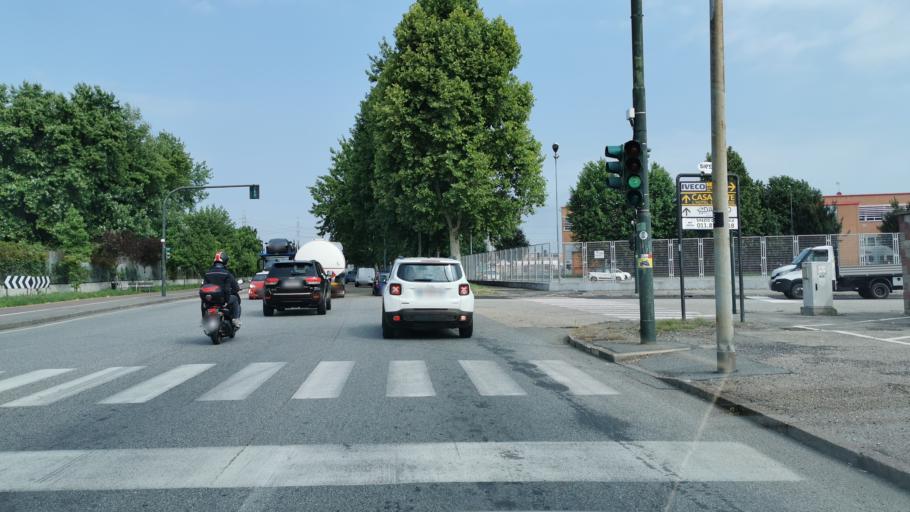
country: IT
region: Piedmont
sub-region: Provincia di Torino
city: Turin
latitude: 45.1052
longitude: 7.7190
